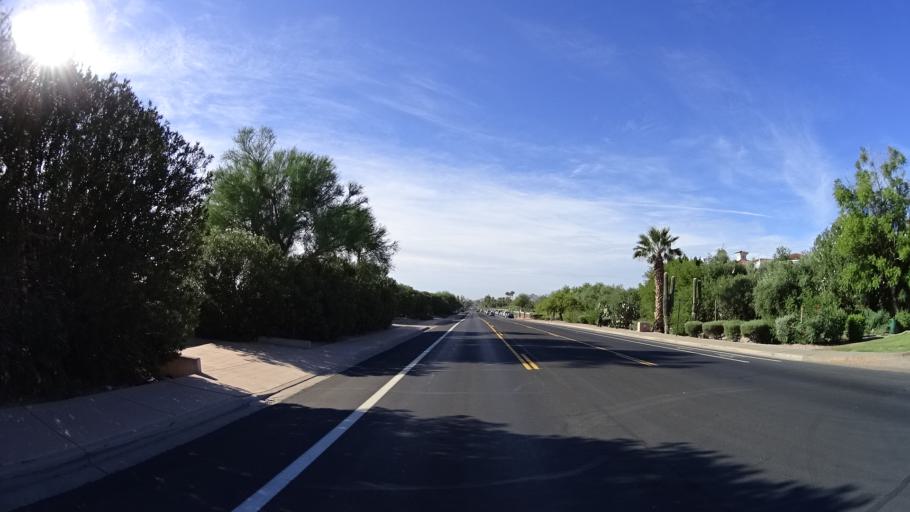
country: US
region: Arizona
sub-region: Maricopa County
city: Paradise Valley
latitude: 33.5122
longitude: -111.9432
